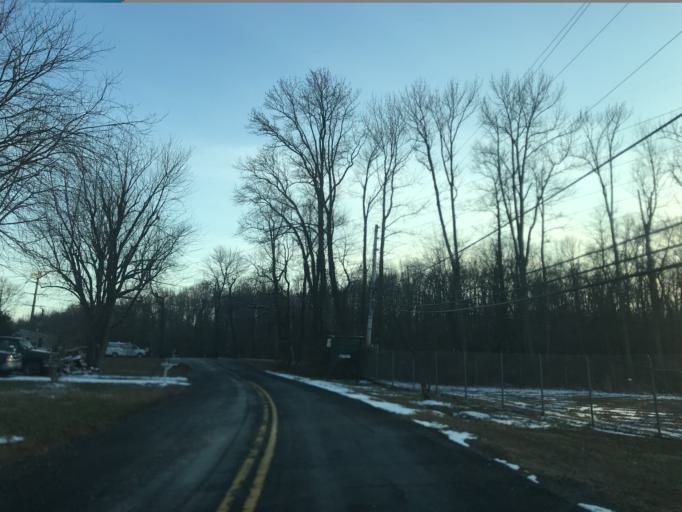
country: US
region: Maryland
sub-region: Harford County
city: Riverside
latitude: 39.4404
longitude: -76.2573
